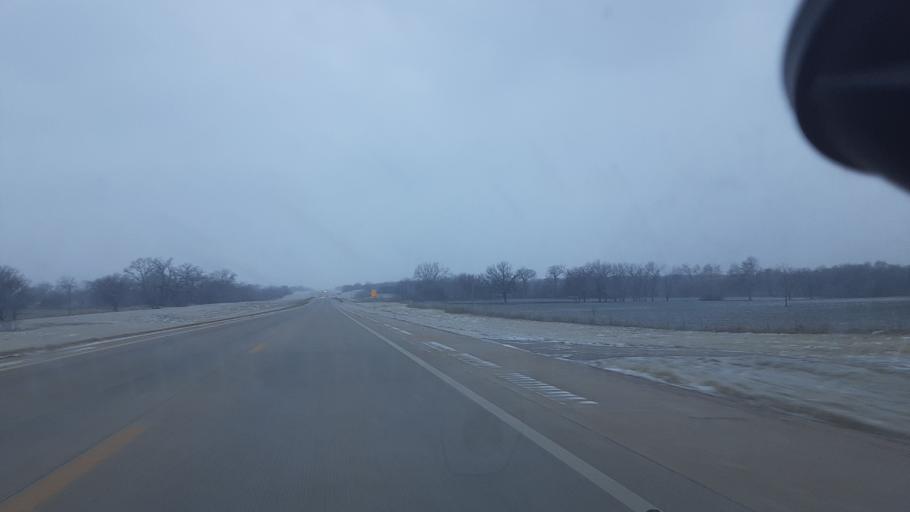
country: US
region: Oklahoma
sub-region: Payne County
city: Perkins
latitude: 35.9859
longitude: -97.1143
